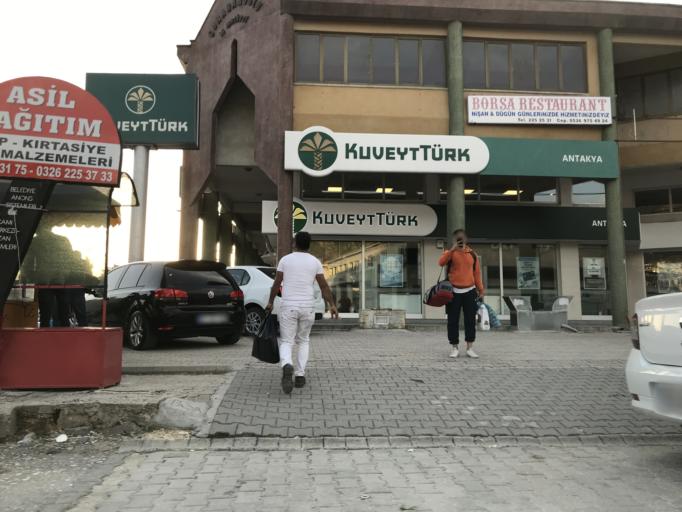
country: TR
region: Hatay
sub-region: Antakya Ilcesi
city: Antakya
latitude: 36.2097
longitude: 36.1637
